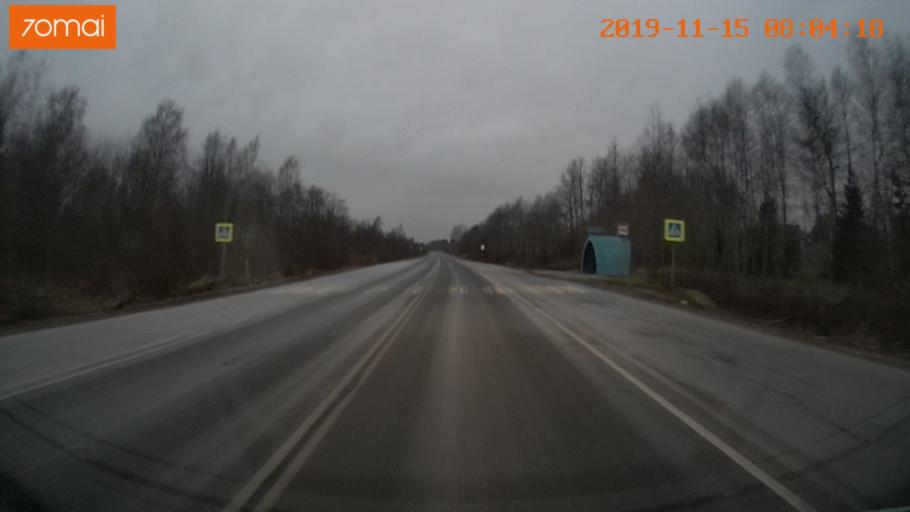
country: RU
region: Vologda
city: Cherepovets
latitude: 59.0066
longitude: 38.0787
